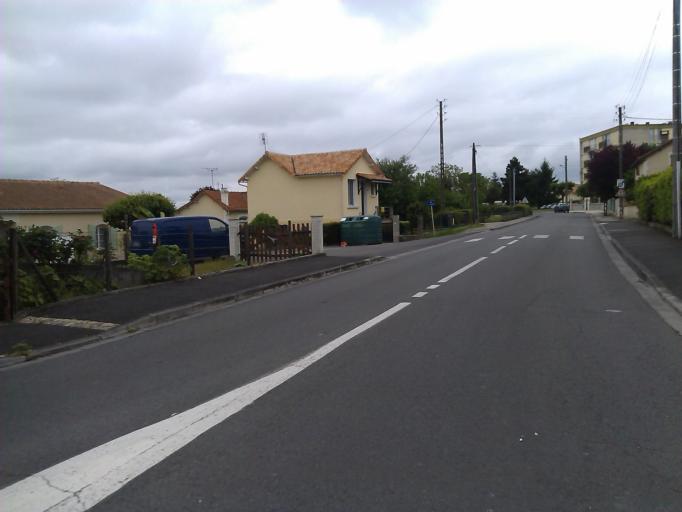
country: FR
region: Poitou-Charentes
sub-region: Departement de la Charente
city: Barbezieux-Saint-Hilaire
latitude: 45.4711
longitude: -0.1500
